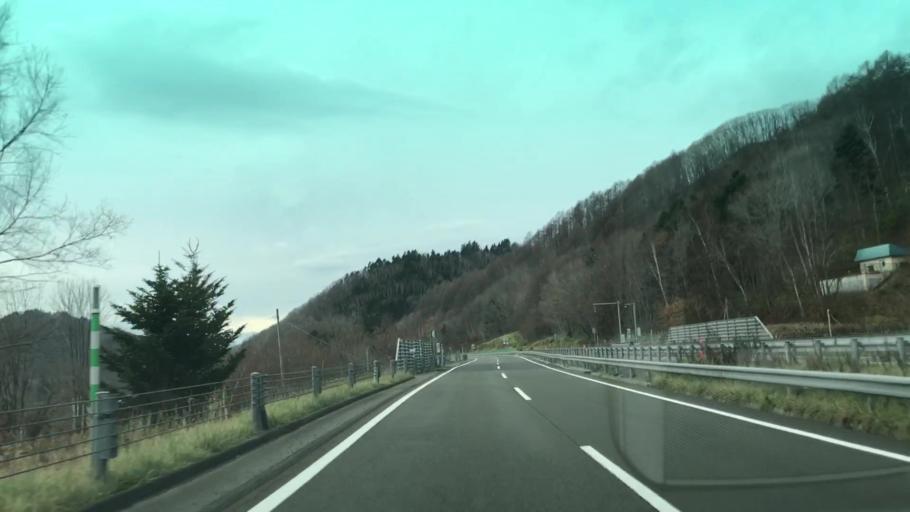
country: JP
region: Hokkaido
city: Chitose
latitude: 42.9061
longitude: 142.0003
